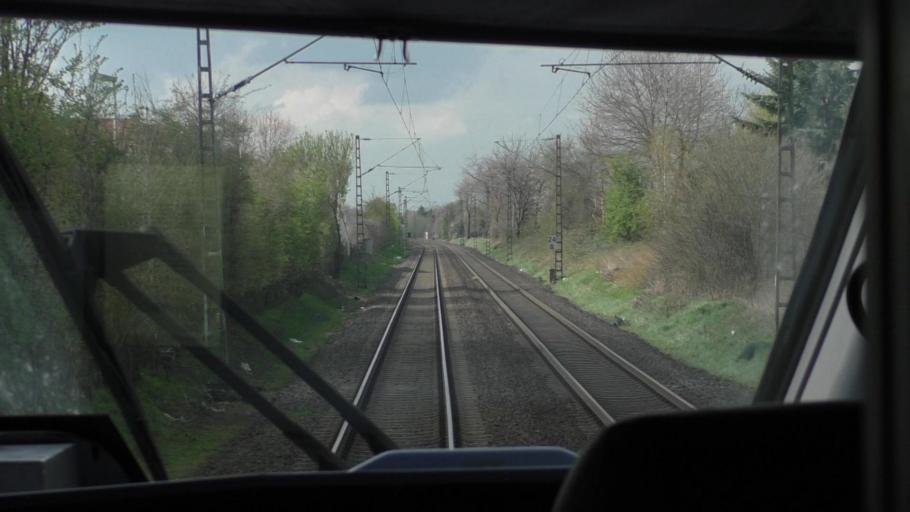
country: DE
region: North Rhine-Westphalia
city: Bornheim
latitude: 50.7588
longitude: 7.0090
